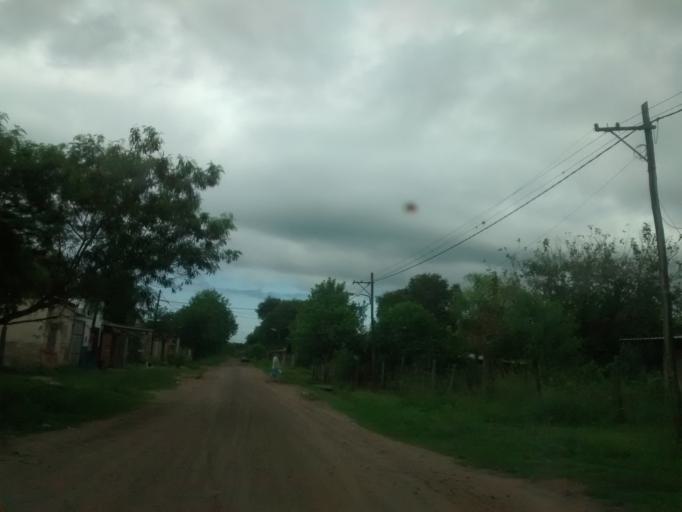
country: AR
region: Chaco
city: Puerto Tirol
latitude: -27.3828
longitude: -59.0868
